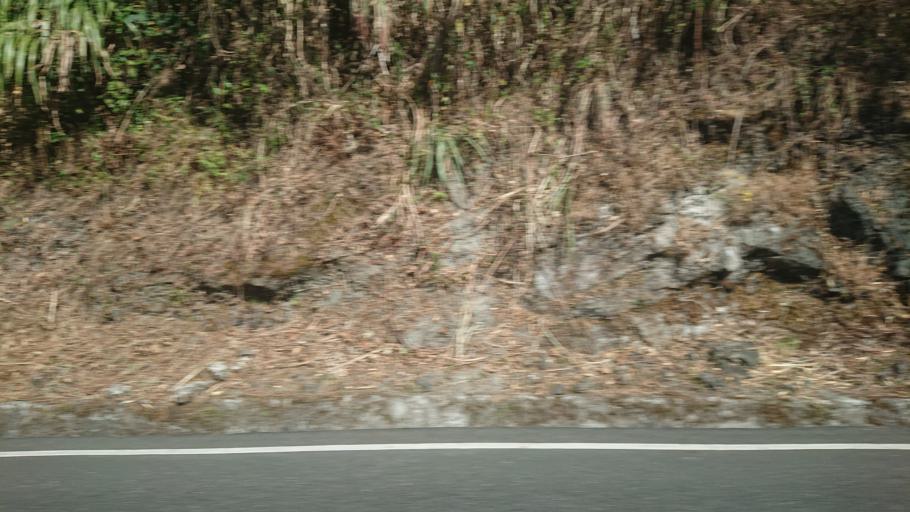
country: TW
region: Taiwan
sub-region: Chiayi
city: Jiayi Shi
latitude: 23.4620
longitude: 120.7255
